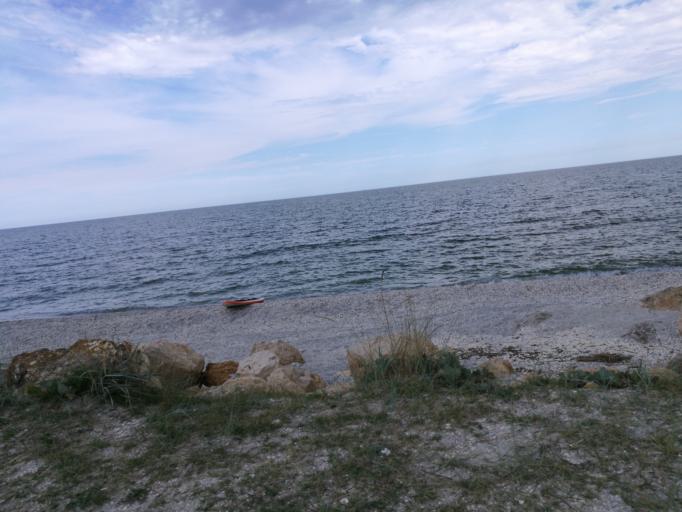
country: RO
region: Constanta
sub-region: Comuna Corbu
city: Corbu
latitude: 44.4300
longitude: 28.7691
